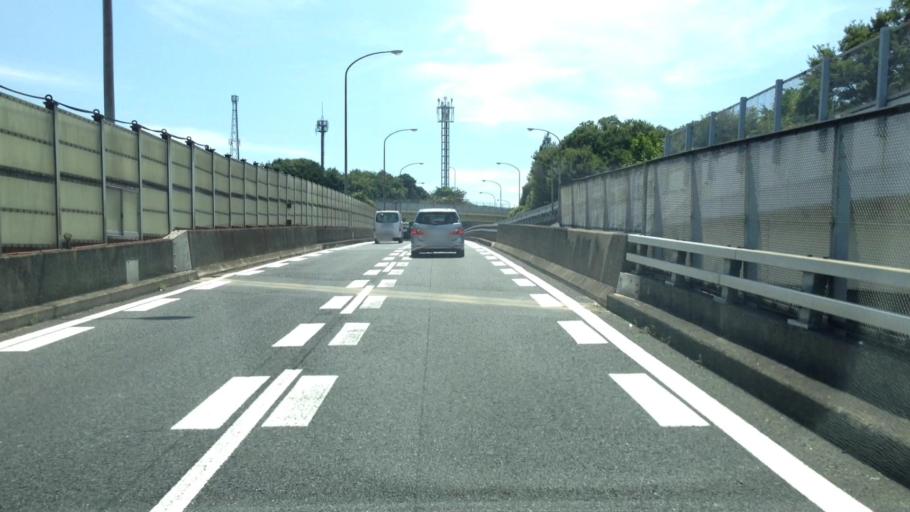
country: JP
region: Kanagawa
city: Yokohama
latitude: 35.4782
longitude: 139.5964
